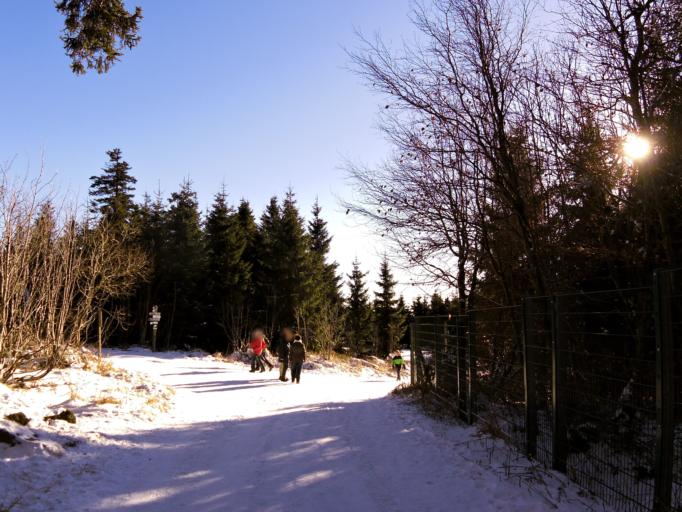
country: DE
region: Bavaria
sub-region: Upper Franconia
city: Bischofsgrun
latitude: 50.0305
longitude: 11.8093
